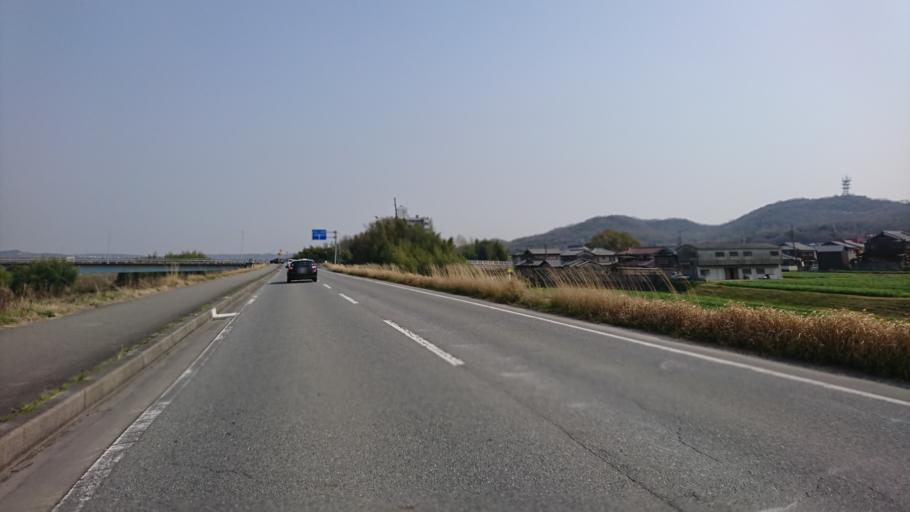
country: JP
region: Hyogo
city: Ono
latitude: 34.8371
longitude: 134.9183
